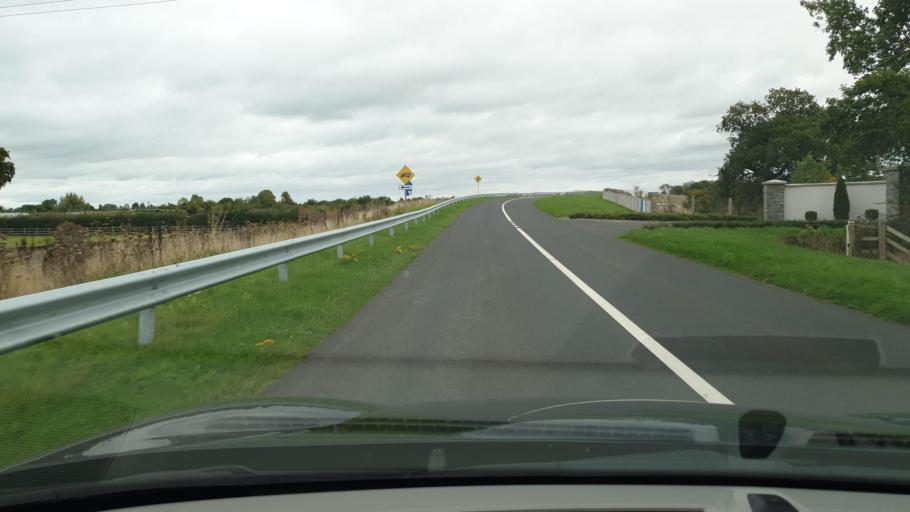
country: IE
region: Leinster
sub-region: Kildare
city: Sallins
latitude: 53.2417
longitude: -6.6798
